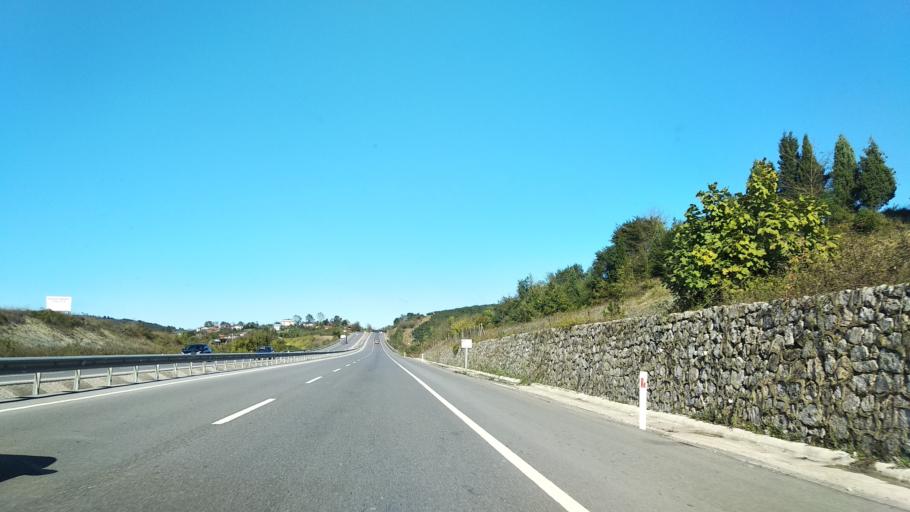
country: TR
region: Sakarya
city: Ortakoy
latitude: 41.0404
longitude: 30.6212
